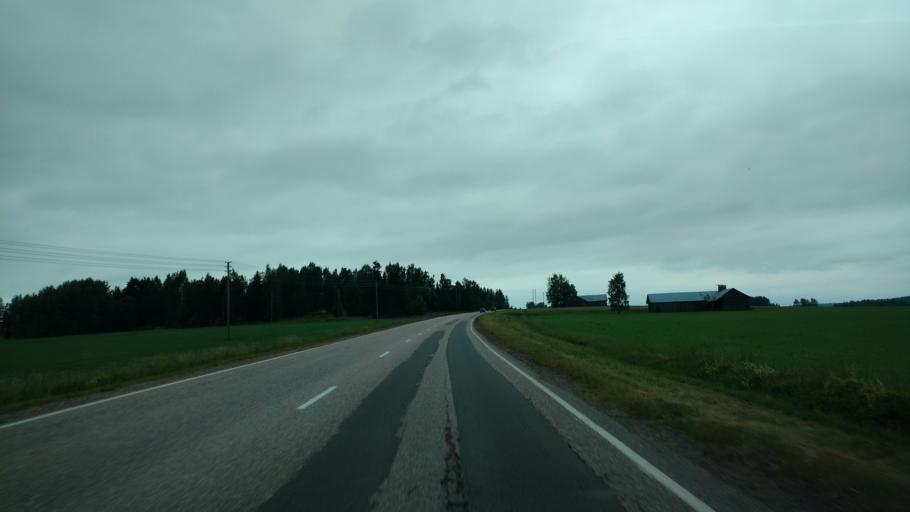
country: FI
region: Varsinais-Suomi
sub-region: Salo
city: Kiikala
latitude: 60.3982
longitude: 23.5838
